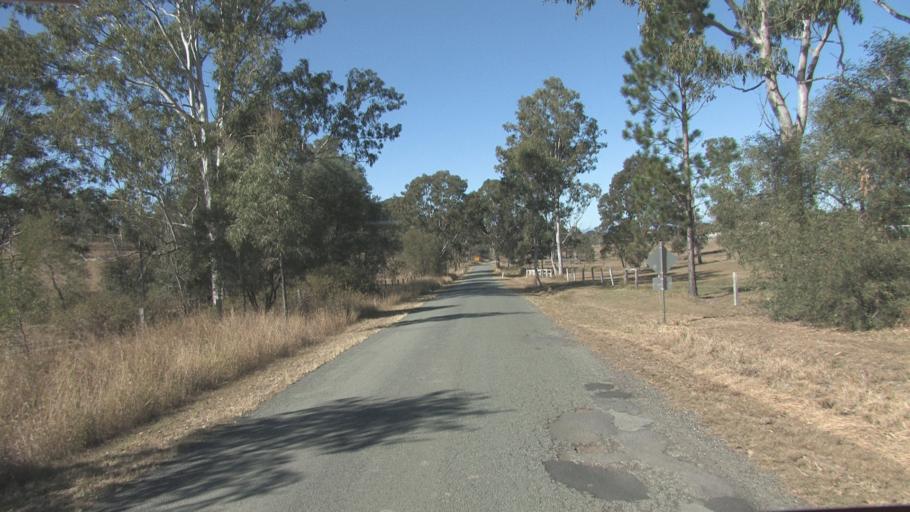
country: AU
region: Queensland
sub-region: Logan
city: Cedar Vale
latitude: -27.8487
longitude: 152.8932
